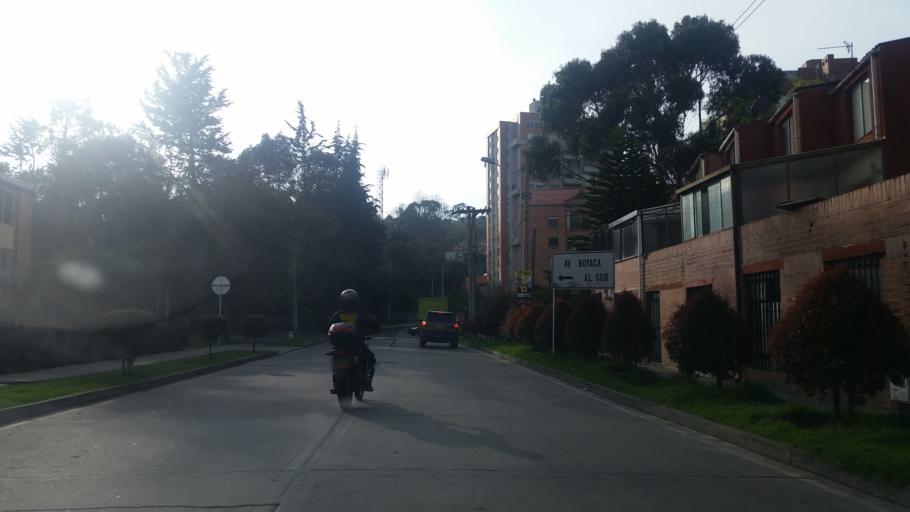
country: CO
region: Cundinamarca
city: Cota
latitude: 4.7512
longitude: -74.0668
